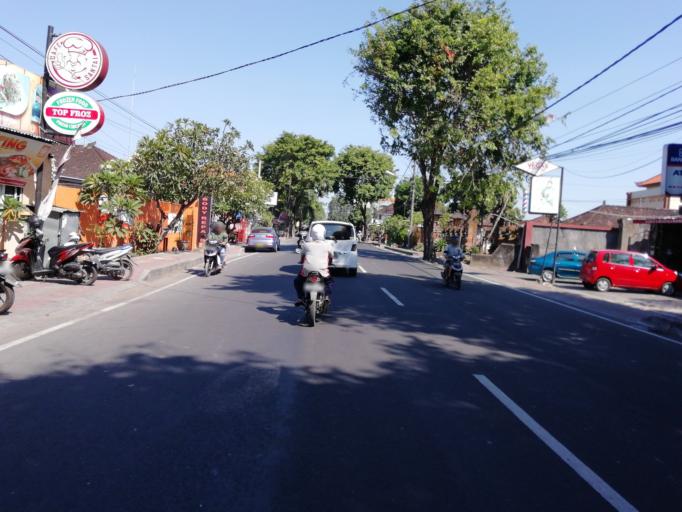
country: ID
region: Bali
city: Karyadharma
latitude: -8.7064
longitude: 115.2203
